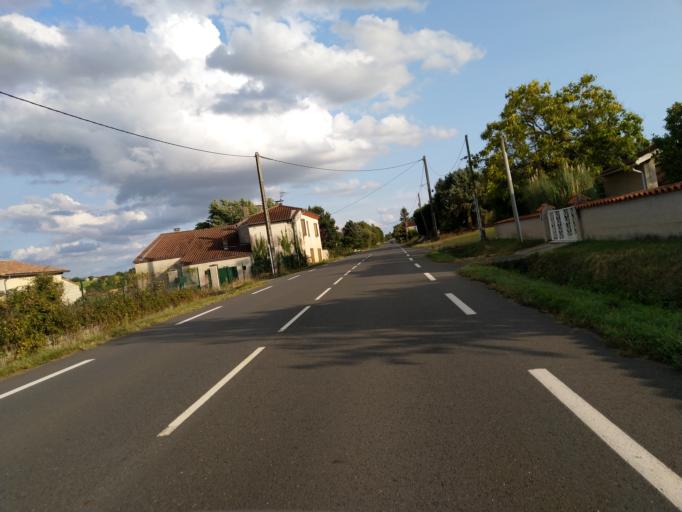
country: FR
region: Midi-Pyrenees
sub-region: Departement du Tarn
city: Frejairolles
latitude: 43.8917
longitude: 2.2195
